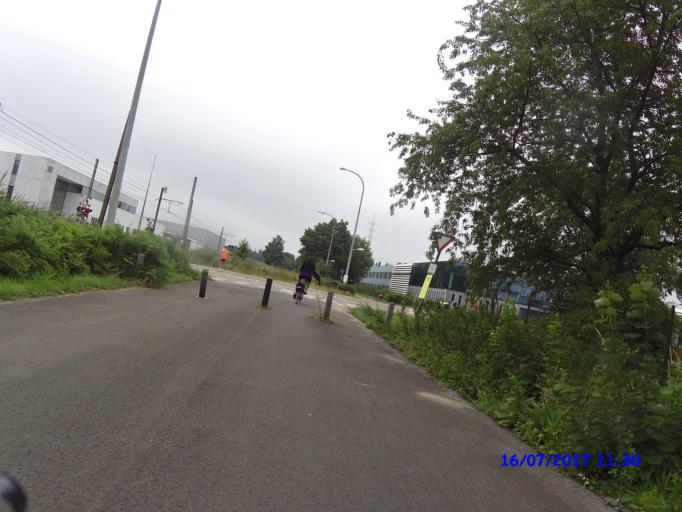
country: BE
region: Flanders
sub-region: Provincie Antwerpen
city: Turnhout
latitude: 51.3016
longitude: 4.9274
